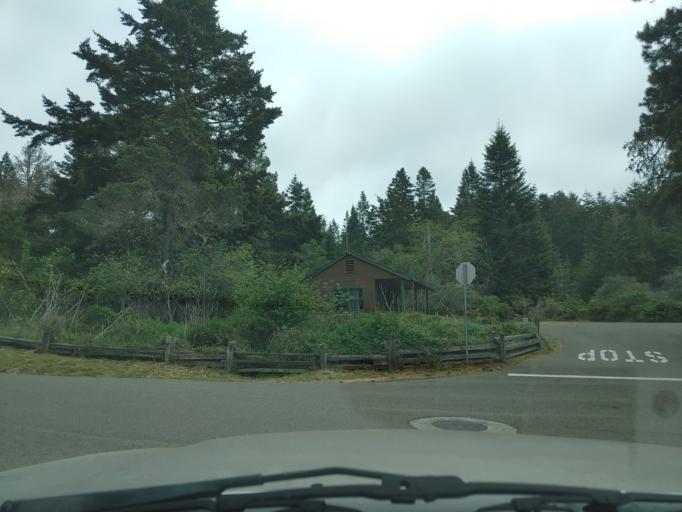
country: US
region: California
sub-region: Mendocino County
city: Fort Bragg
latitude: 39.3306
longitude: -123.8057
